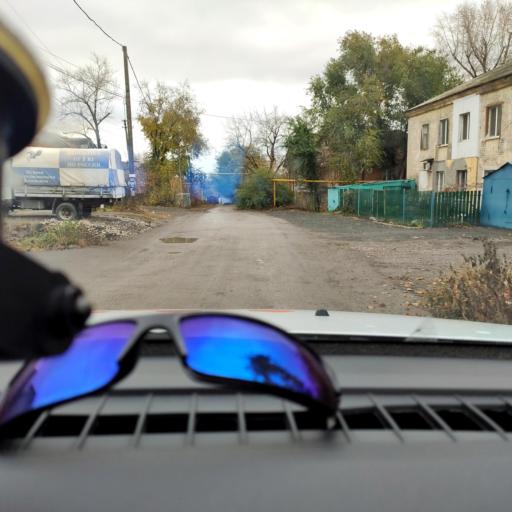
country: RU
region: Samara
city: Samara
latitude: 53.1731
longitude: 50.1753
